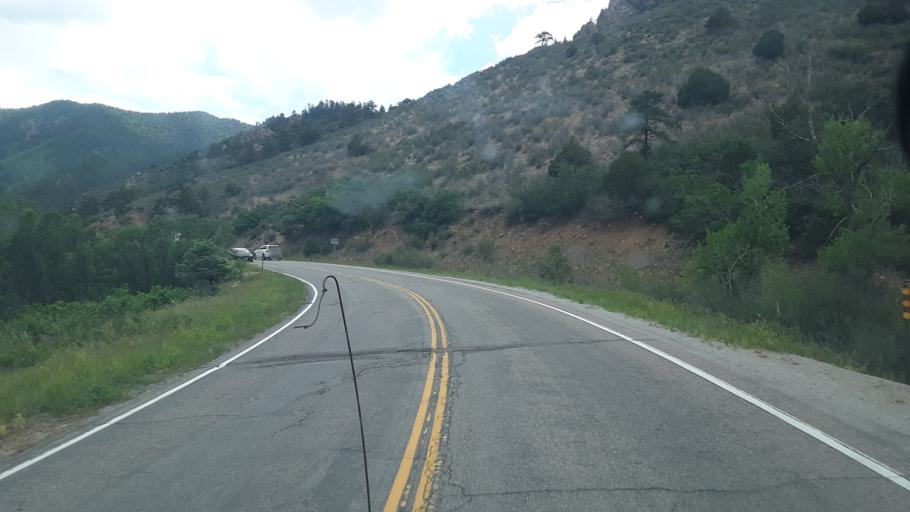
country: US
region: Colorado
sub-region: Fremont County
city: Florence
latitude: 38.1751
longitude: -105.1522
